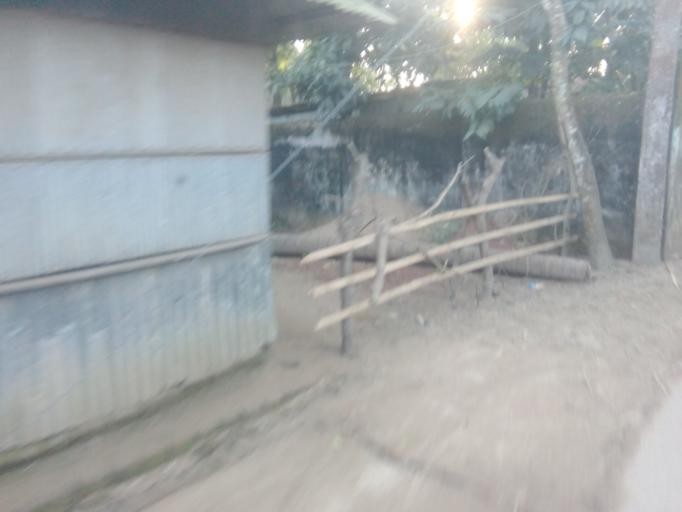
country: BD
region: Chittagong
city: Comilla
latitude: 23.4120
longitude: 91.2317
